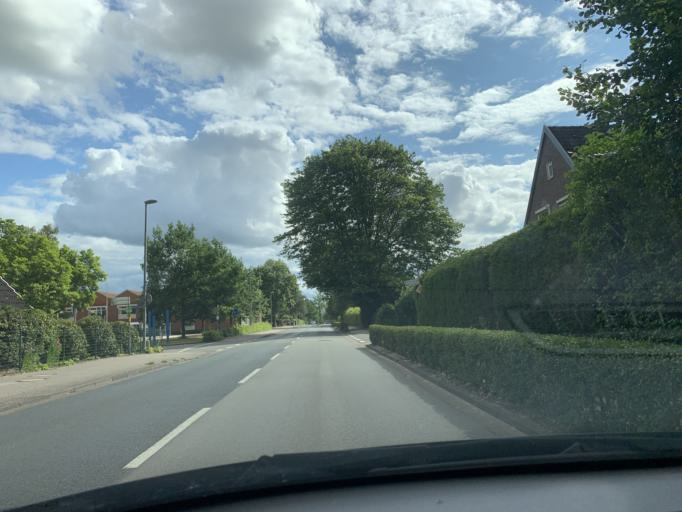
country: DE
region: Lower Saxony
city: Bad Zwischenahn
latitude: 53.1981
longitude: 7.9925
